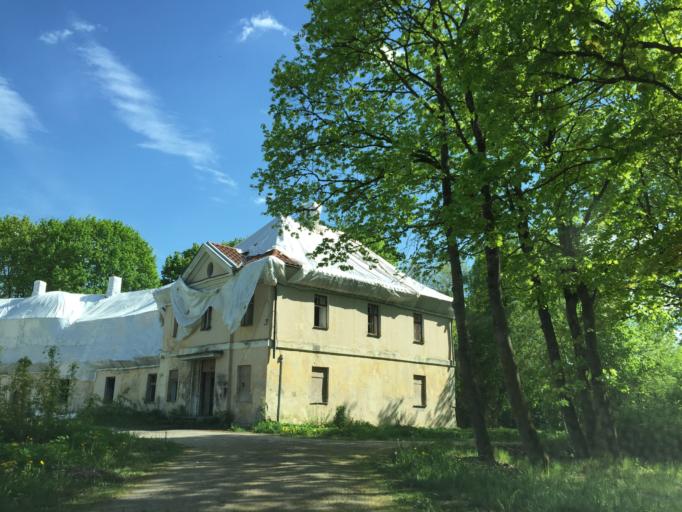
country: LV
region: Bauskas Rajons
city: Bauska
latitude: 56.3922
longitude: 24.1294
